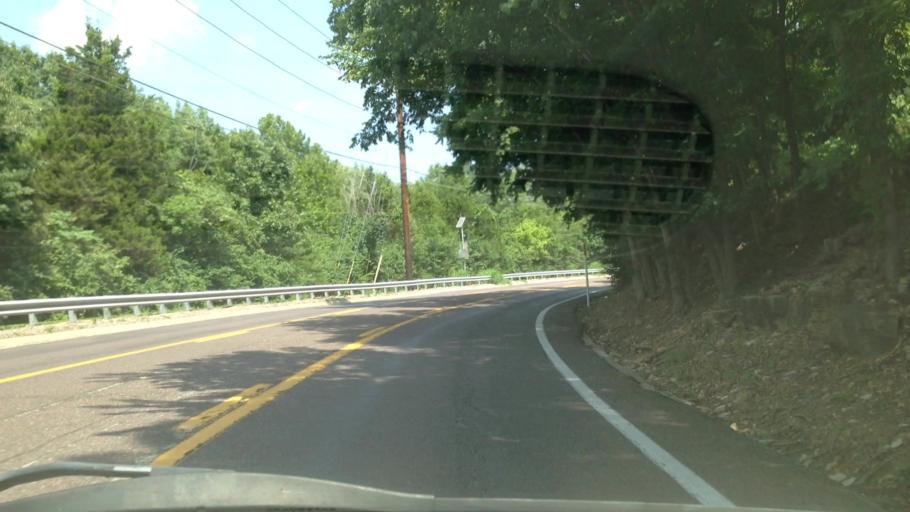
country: US
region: Missouri
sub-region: Saint Louis County
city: Des Peres
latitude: 38.5866
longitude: -90.4453
